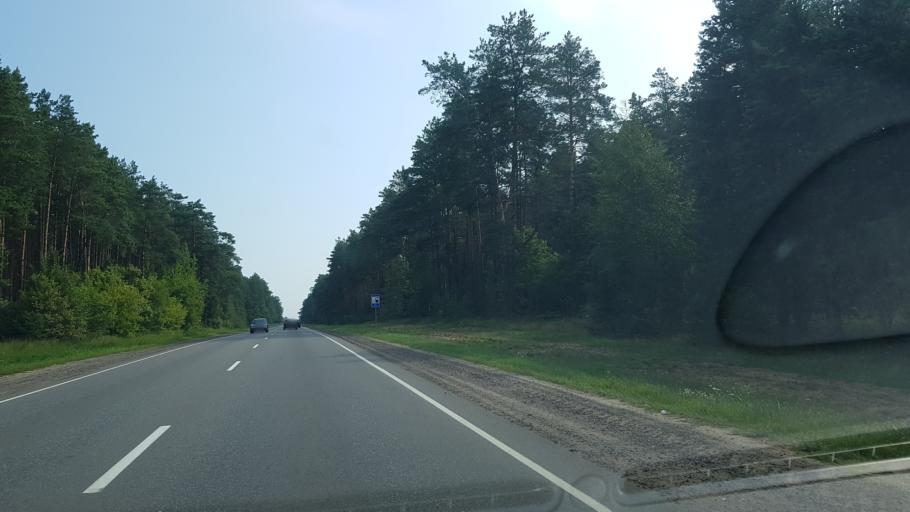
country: BY
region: Mogilev
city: Babruysk
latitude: 53.1628
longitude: 29.3250
